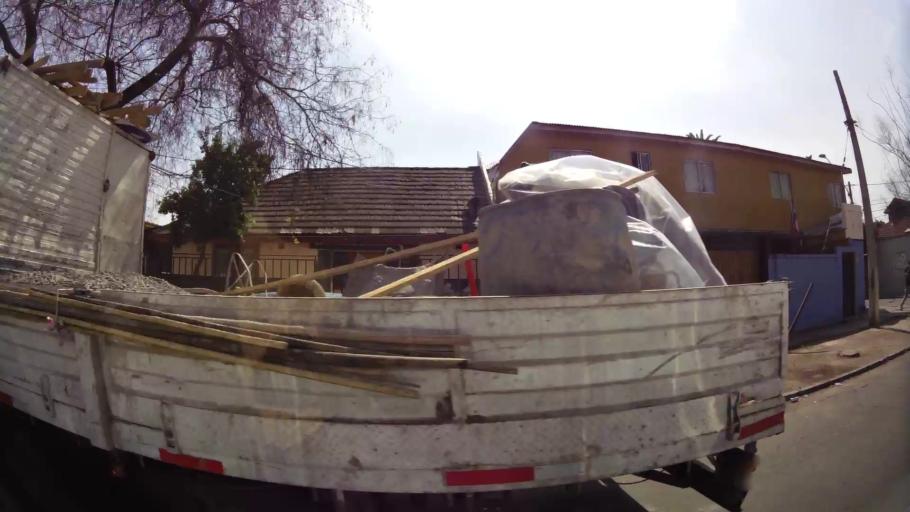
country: CL
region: Santiago Metropolitan
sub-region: Provincia de Santiago
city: Lo Prado
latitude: -33.4173
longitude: -70.6956
